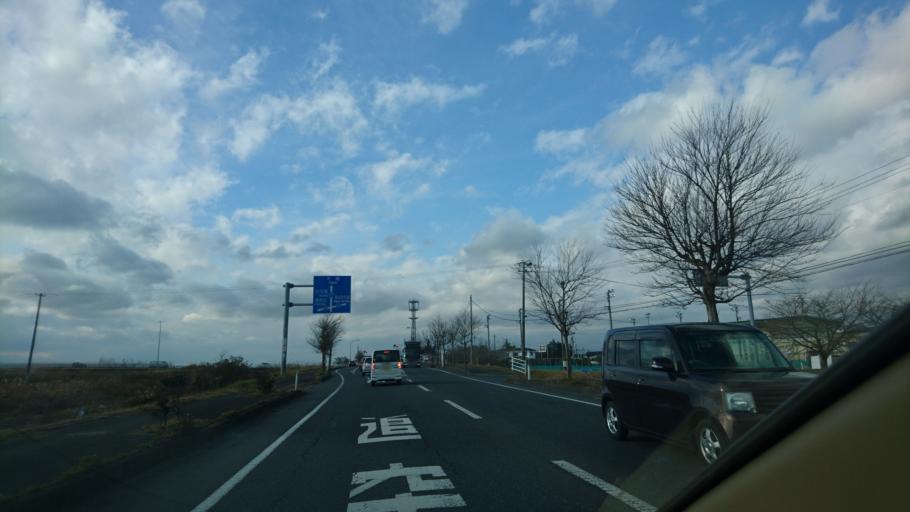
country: JP
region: Miyagi
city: Wakuya
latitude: 38.5299
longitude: 141.1334
